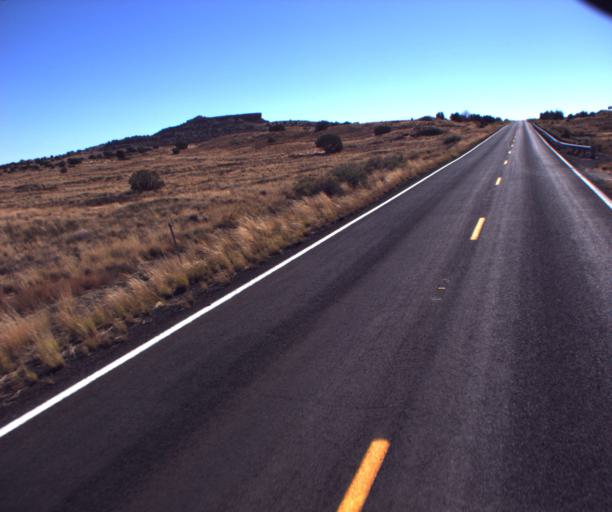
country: US
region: Arizona
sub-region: Navajo County
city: First Mesa
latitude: 35.9647
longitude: -110.6903
